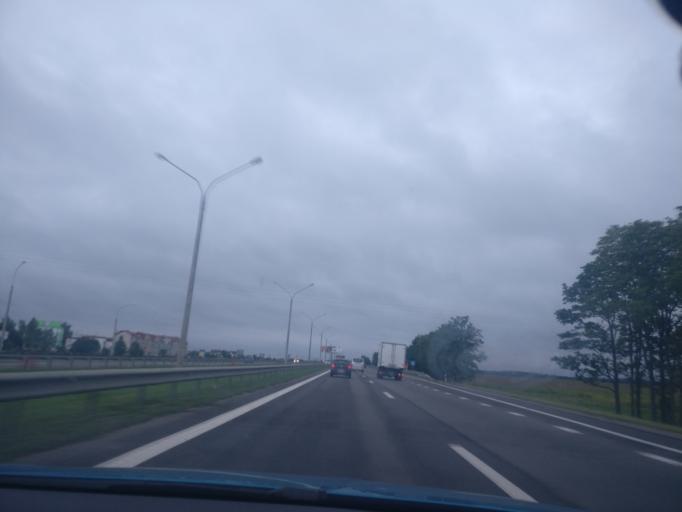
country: BY
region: Minsk
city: Slabada
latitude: 54.0131
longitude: 27.8749
